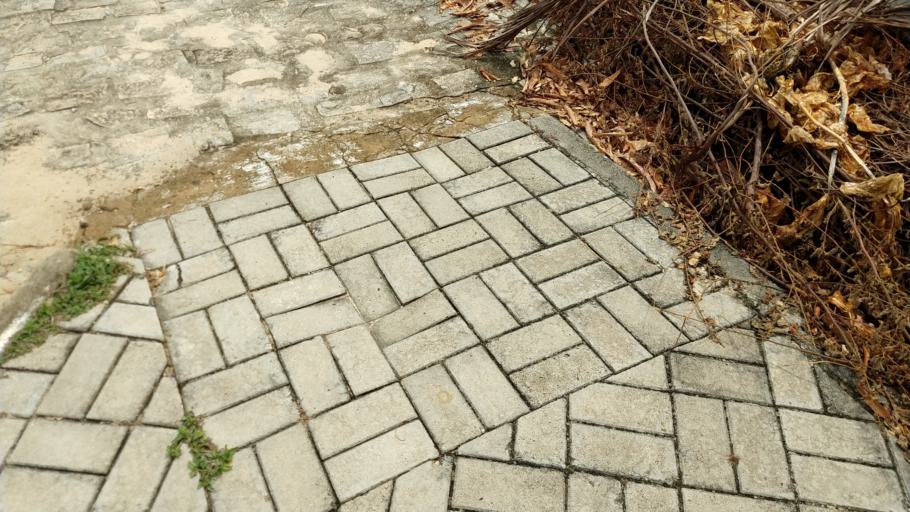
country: BR
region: Ceara
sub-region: Fortaleza
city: Fortaleza
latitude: -3.7463
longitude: -38.5746
